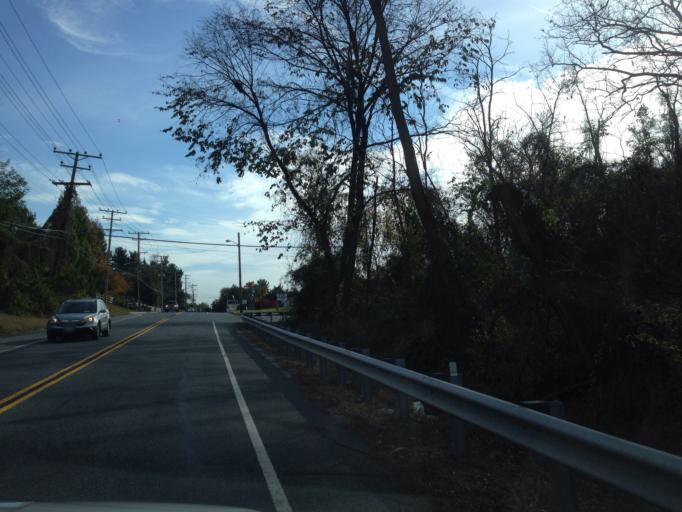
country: US
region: Maryland
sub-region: Baltimore County
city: Hunt Valley
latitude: 39.5314
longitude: -76.6459
